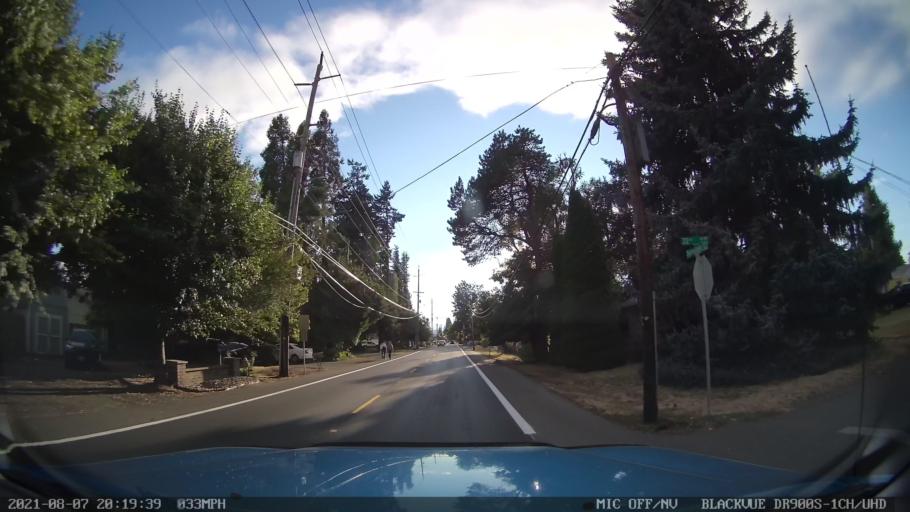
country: US
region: Oregon
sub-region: Marion County
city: Four Corners
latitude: 44.9540
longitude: -122.9952
